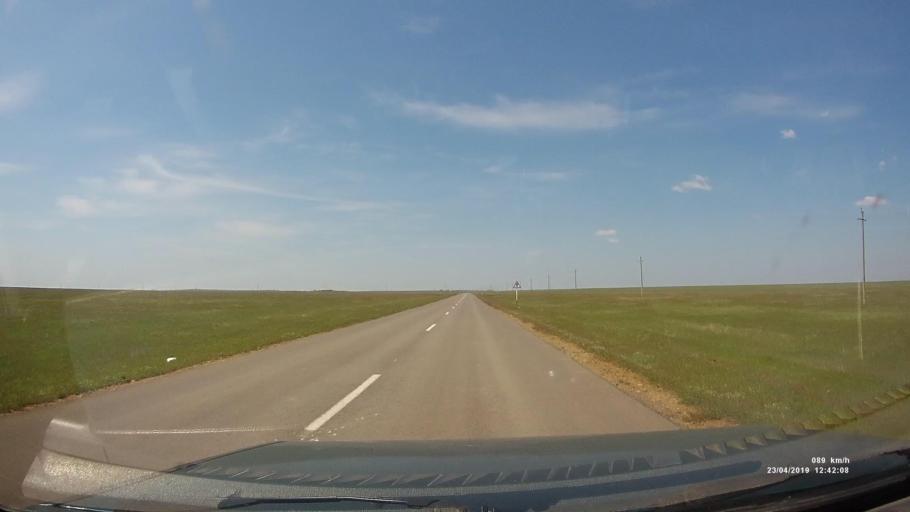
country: RU
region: Kalmykiya
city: Yashalta
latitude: 46.4535
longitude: 42.6703
